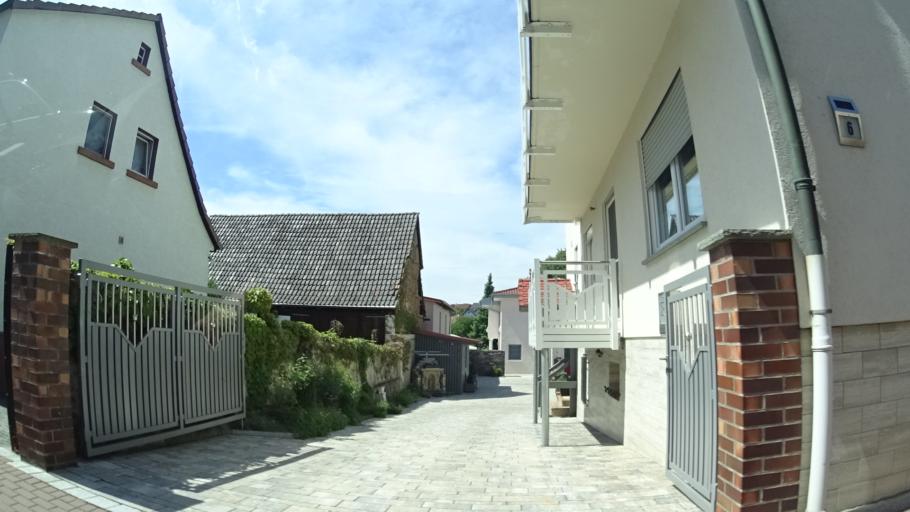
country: DE
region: Bavaria
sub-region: Regierungsbezirk Unterfranken
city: Arnstein
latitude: 50.0178
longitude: 10.0062
